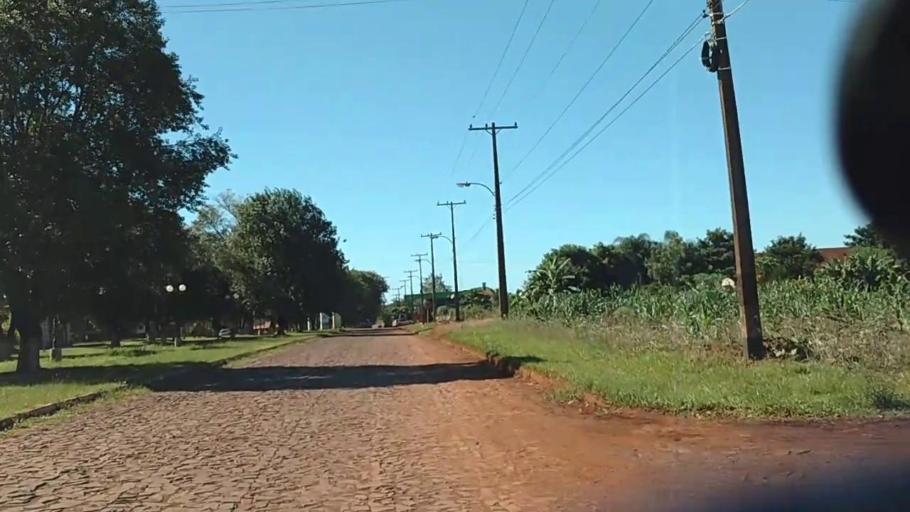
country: PY
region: Alto Parana
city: Naranjal
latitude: -25.9726
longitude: -55.1963
